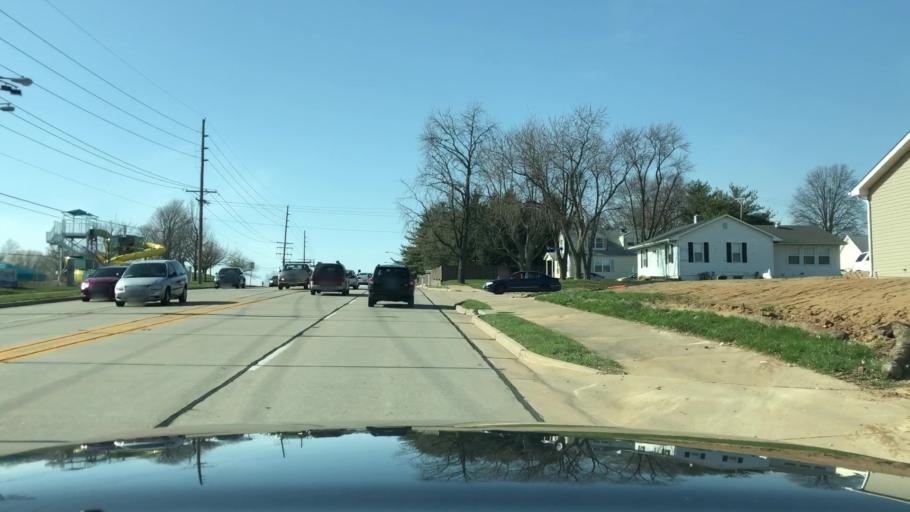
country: US
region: Missouri
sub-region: Saint Charles County
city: Saint Charles
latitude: 38.7673
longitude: -90.5456
